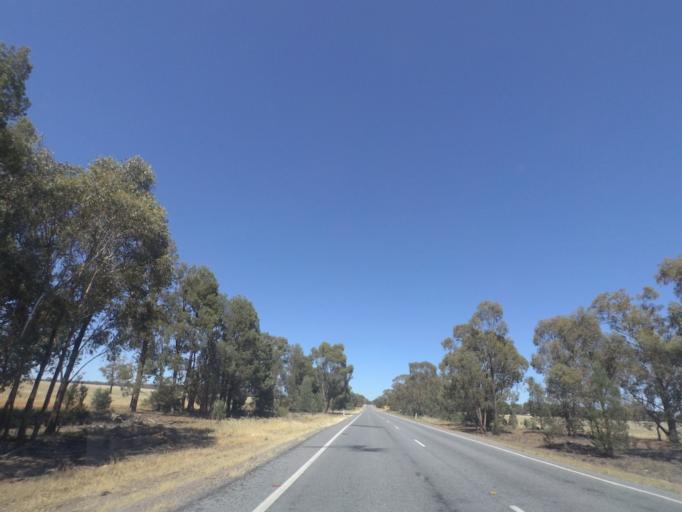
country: AU
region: New South Wales
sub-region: Narrandera
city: Narrandera
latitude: -34.4164
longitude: 146.8575
